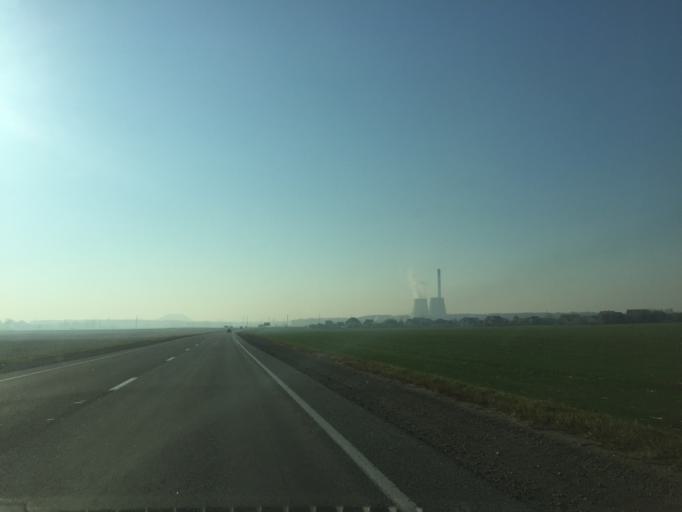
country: BY
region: Gomel
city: Kastsyukowka
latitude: 52.4691
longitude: 30.8237
